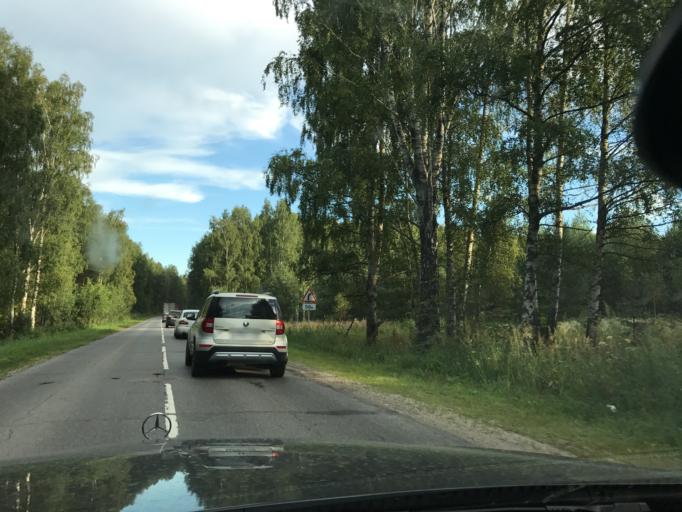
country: RU
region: Vladimir
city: Raduzhnyy
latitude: 56.0002
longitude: 40.2676
